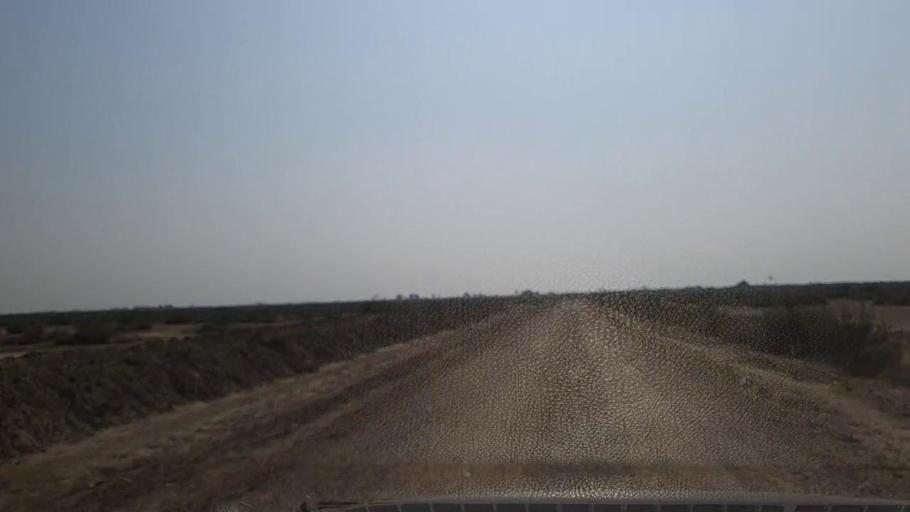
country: PK
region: Sindh
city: Mirpur Sakro
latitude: 24.4281
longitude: 67.7183
